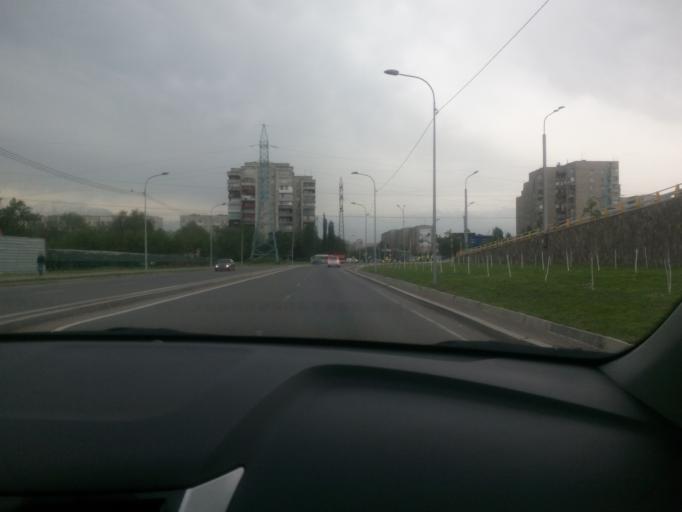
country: KZ
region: Almaty Qalasy
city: Almaty
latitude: 43.2430
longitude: 76.8284
